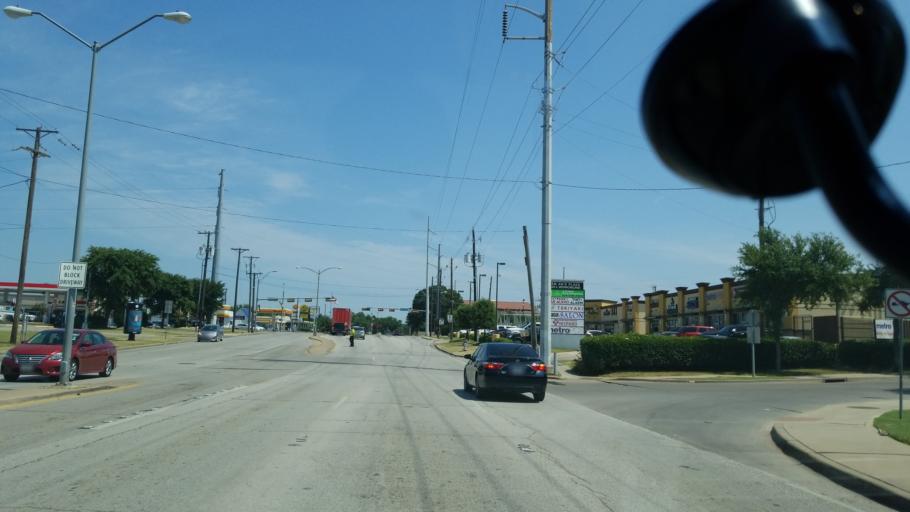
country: US
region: Texas
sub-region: Dallas County
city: Cockrell Hill
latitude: 32.7190
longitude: -96.8742
